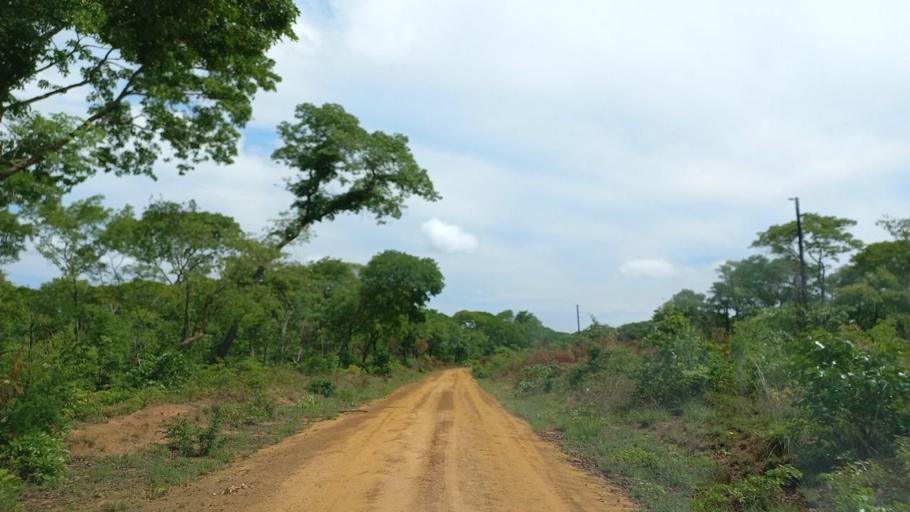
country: ZM
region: North-Western
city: Kabompo
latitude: -13.5387
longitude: 24.0986
